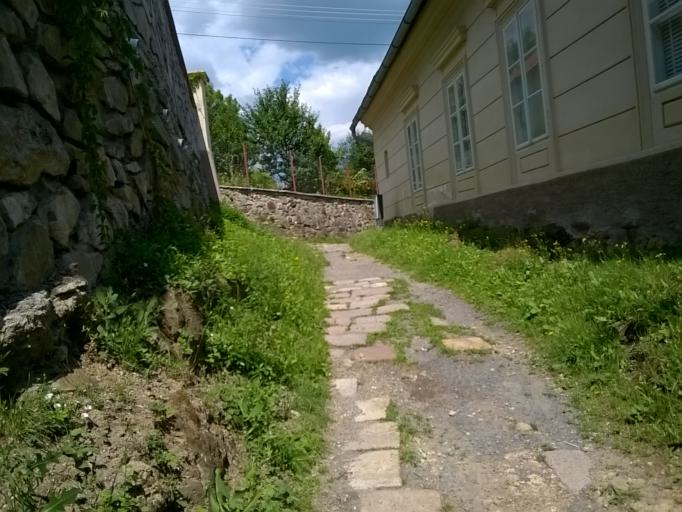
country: SK
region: Banskobystricky
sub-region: Okres Banska Bystrica
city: Banska Stiavnica
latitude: 48.4582
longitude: 18.8997
